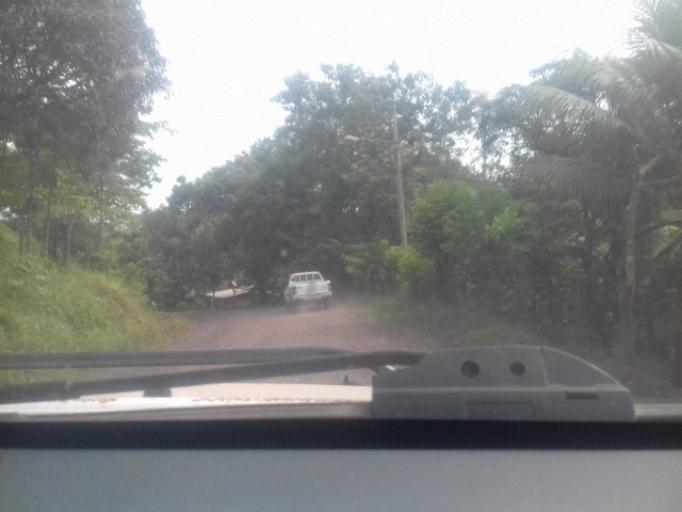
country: NI
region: Atlantico Norte (RAAN)
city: Waslala
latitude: 13.4094
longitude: -85.3196
